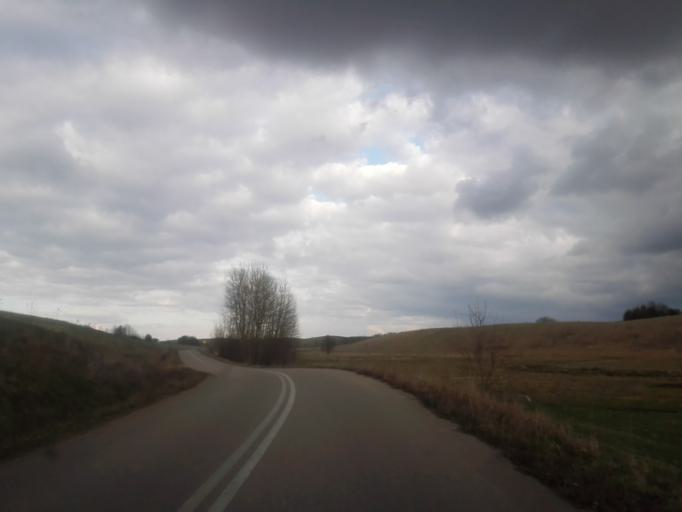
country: PL
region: Podlasie
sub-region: Suwalki
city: Suwalki
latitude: 54.2004
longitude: 22.9836
